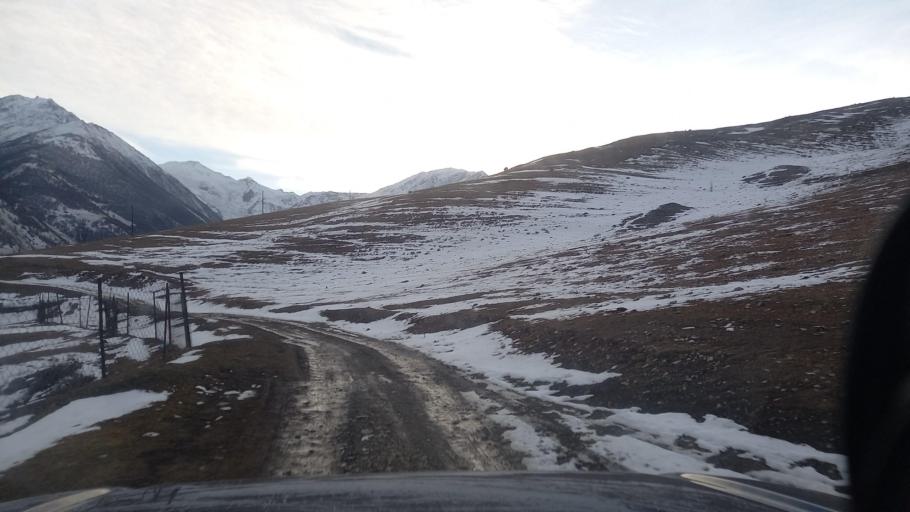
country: RU
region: Ingushetiya
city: Dzhayrakh
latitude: 42.8497
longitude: 44.5129
